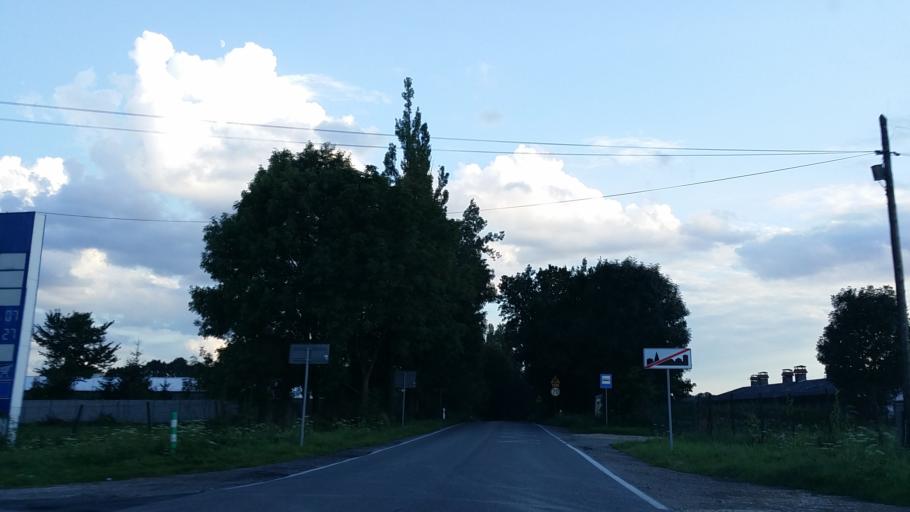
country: PL
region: Lesser Poland Voivodeship
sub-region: Powiat oswiecimski
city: Przeciszow
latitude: 49.9963
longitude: 19.3646
